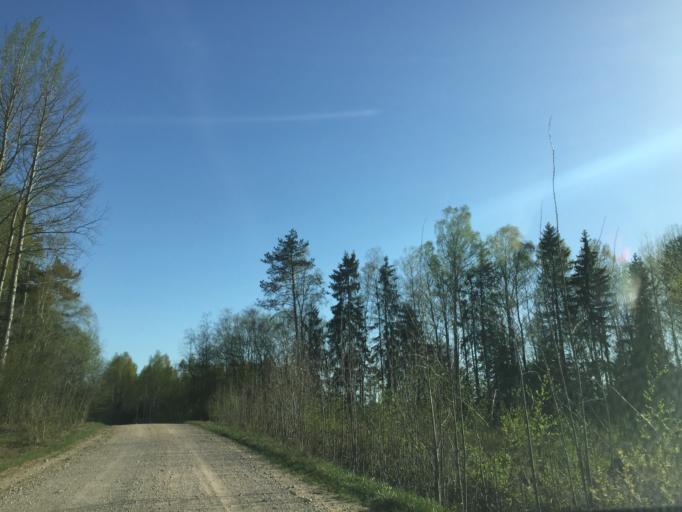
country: LV
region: Ergli
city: Ergli
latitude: 56.8914
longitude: 25.4910
